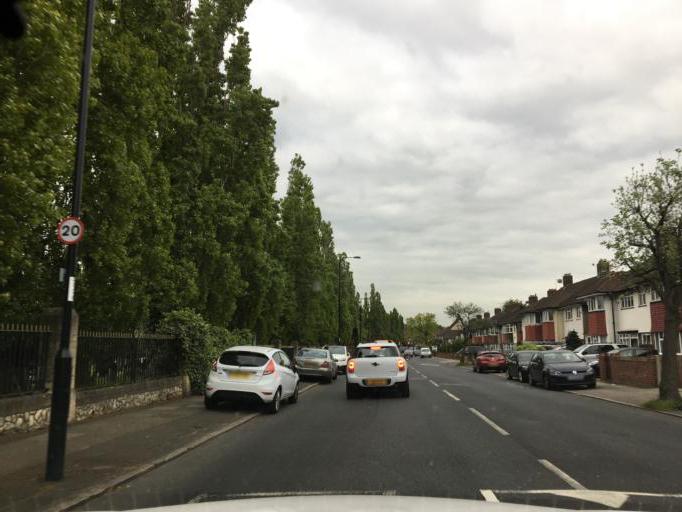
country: GB
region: England
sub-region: Greater London
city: Blackheath
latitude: 51.4360
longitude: 0.0078
